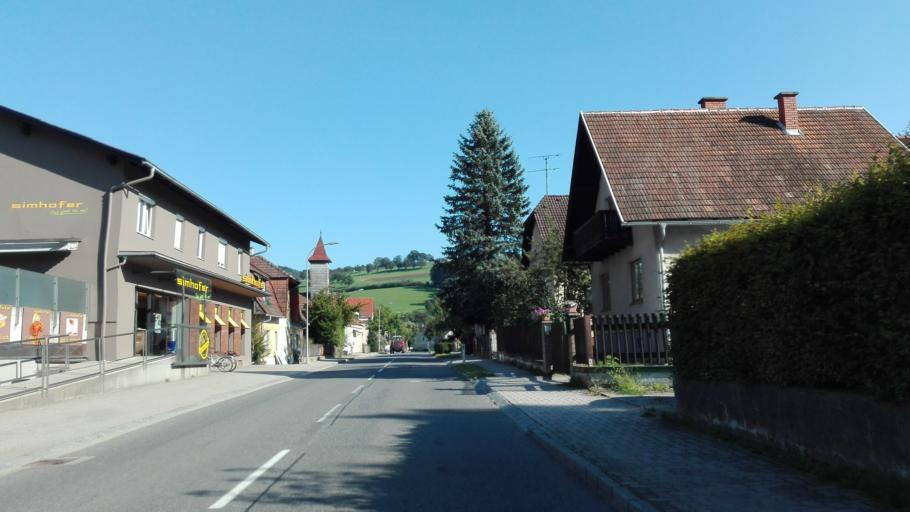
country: AT
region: Lower Austria
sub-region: Politischer Bezirk Sankt Polten
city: Altlengbach
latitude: 48.1359
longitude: 15.9115
